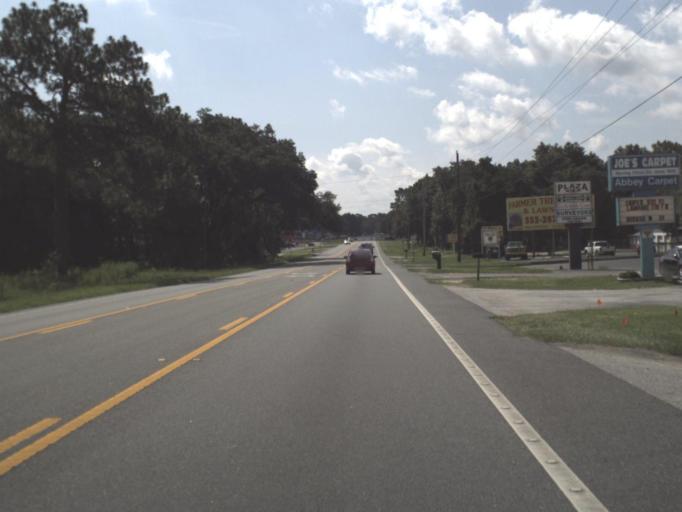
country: US
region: Florida
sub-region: Citrus County
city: Inverness Highlands North
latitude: 28.8635
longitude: -82.3545
